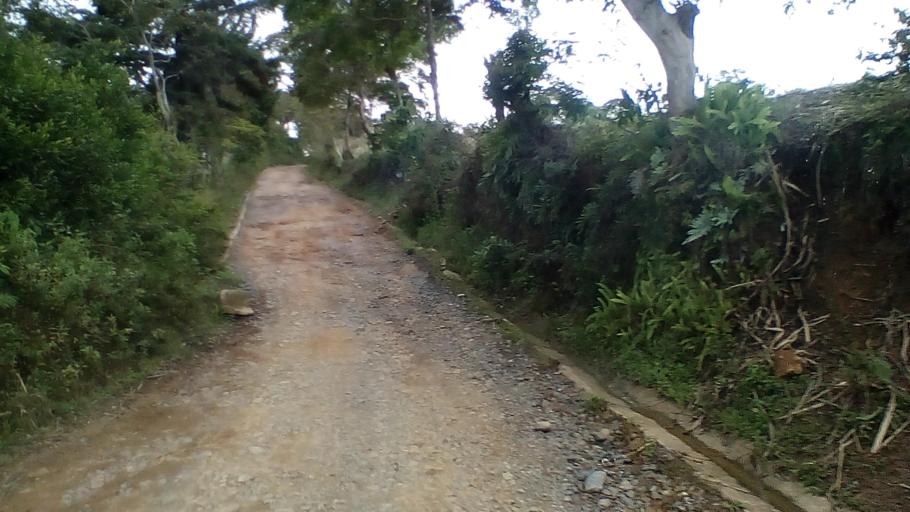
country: CO
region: Boyaca
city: Santana
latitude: 6.0151
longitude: -73.5120
